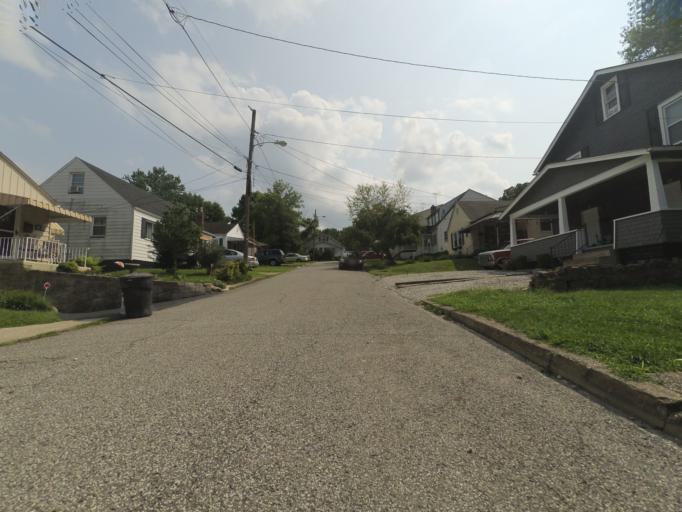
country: US
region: West Virginia
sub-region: Cabell County
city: Huntington
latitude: 38.4050
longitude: -82.4051
